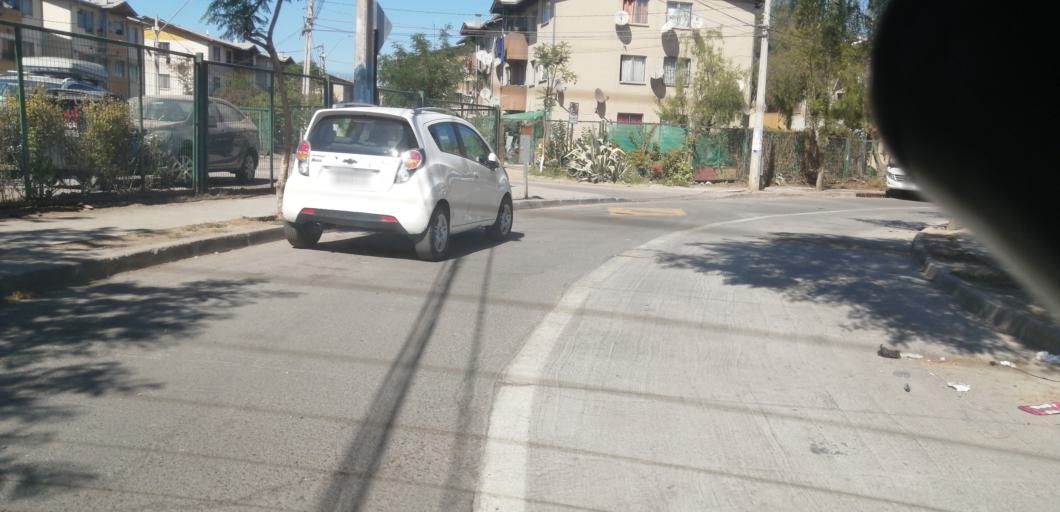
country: CL
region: Santiago Metropolitan
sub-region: Provincia de Santiago
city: Lo Prado
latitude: -33.4409
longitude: -70.7659
